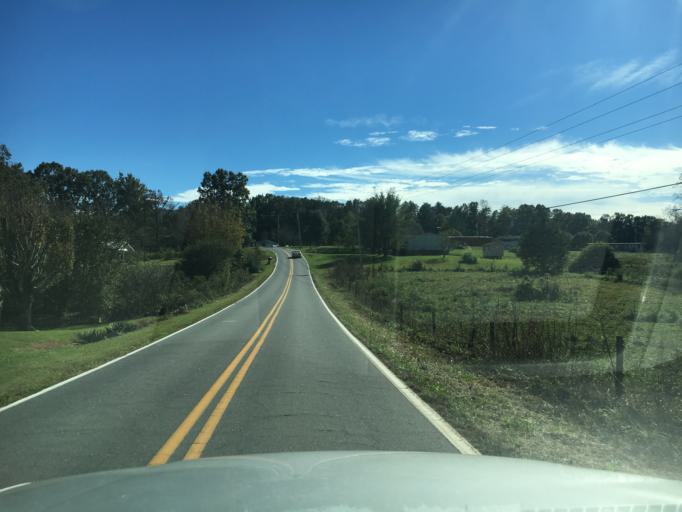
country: US
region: North Carolina
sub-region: Burke County
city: Salem
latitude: 35.6884
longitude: -81.7331
